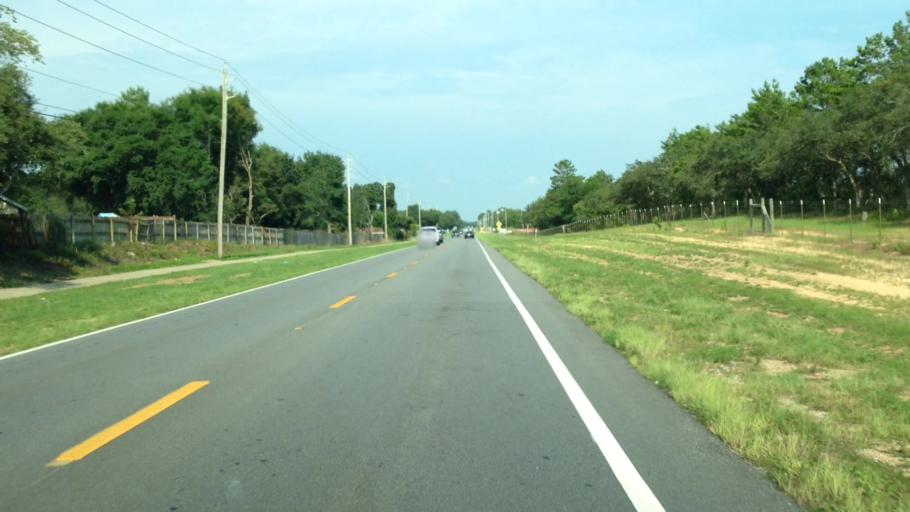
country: US
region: Florida
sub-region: Santa Rosa County
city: Holley
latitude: 30.4326
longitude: -86.8871
